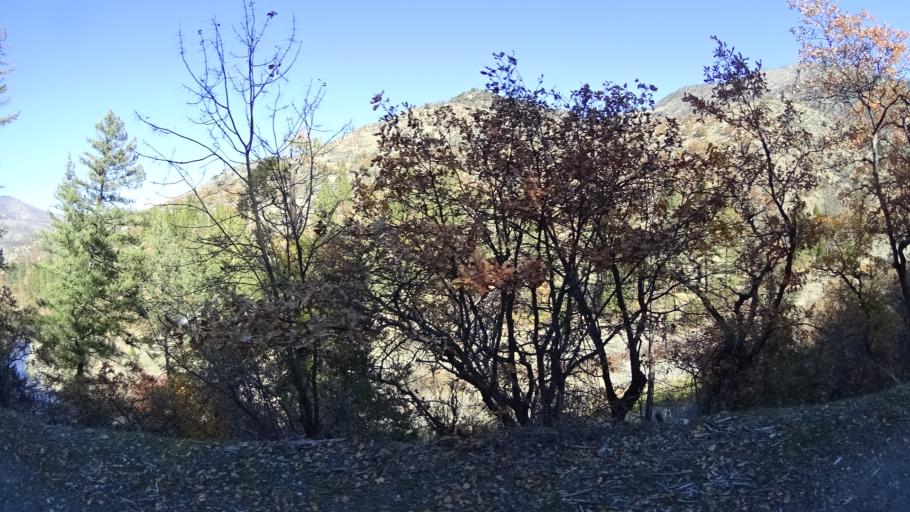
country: US
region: California
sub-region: Siskiyou County
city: Yreka
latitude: 41.8645
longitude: -122.8008
